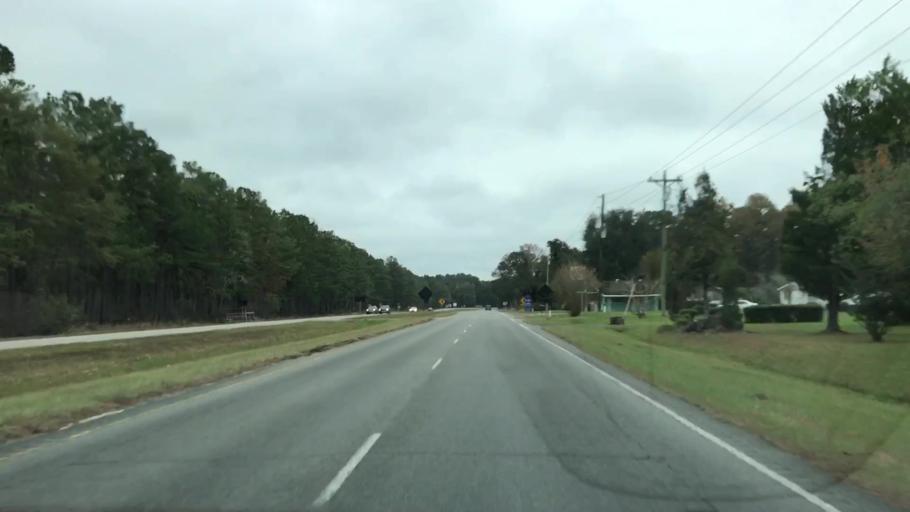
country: US
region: South Carolina
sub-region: Charleston County
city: Awendaw
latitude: 33.0333
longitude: -79.6218
